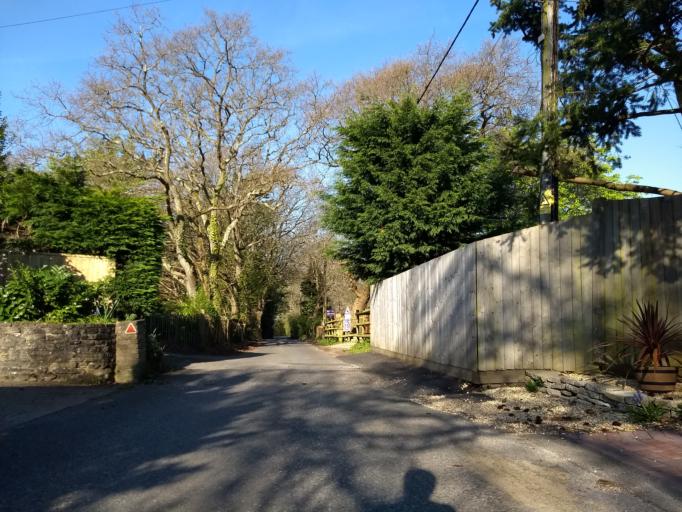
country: GB
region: England
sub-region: Isle of Wight
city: Ryde
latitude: 50.7291
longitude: -1.2165
